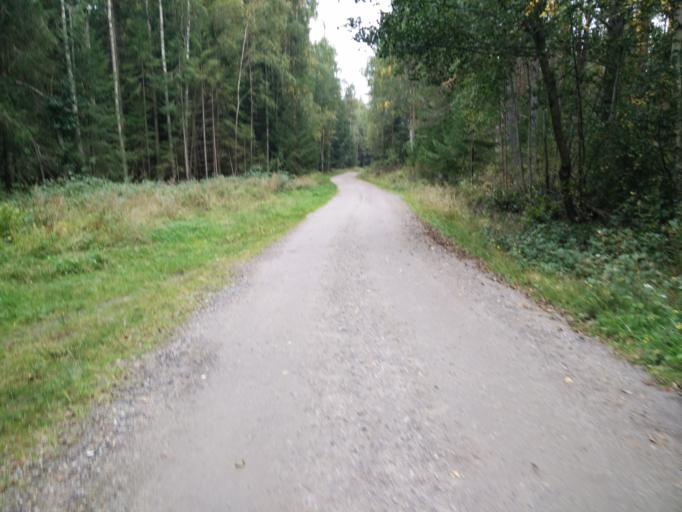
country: SE
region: Gaevleborg
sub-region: Hudiksvalls Kommun
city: Hudiksvall
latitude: 61.8327
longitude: 17.3365
